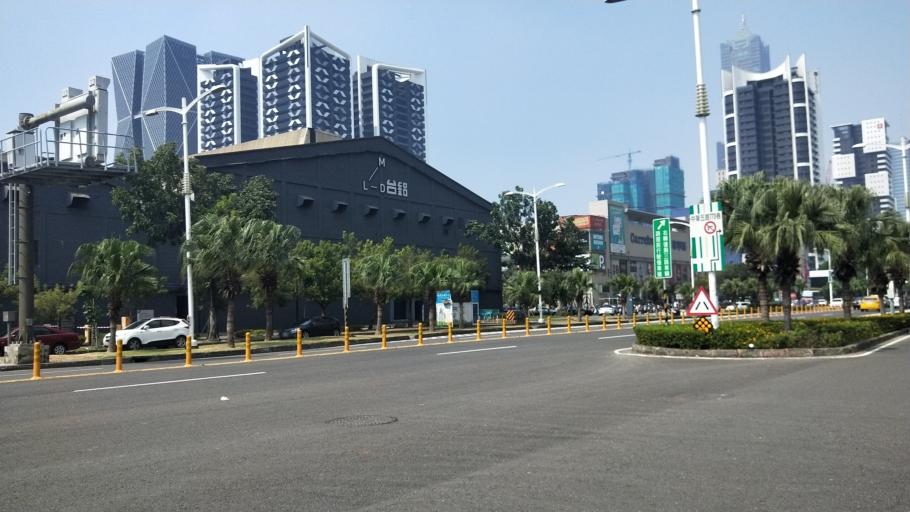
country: TW
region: Kaohsiung
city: Kaohsiung
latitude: 22.6040
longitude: 120.3059
